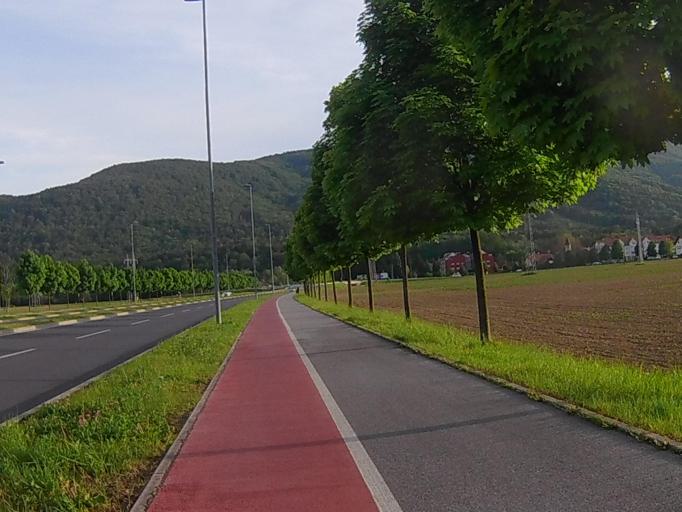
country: SI
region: Maribor
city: Pekre
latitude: 46.5411
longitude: 15.6173
